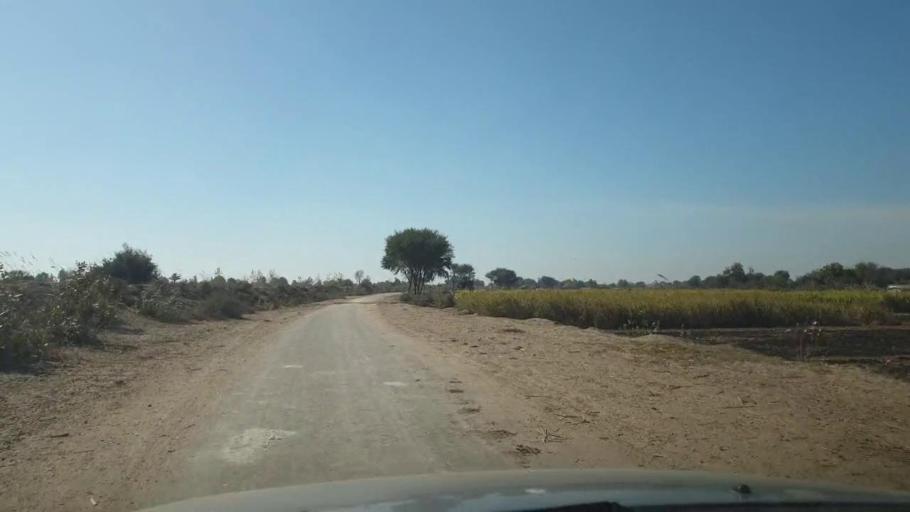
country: PK
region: Sindh
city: Ghotki
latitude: 28.0181
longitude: 69.2673
